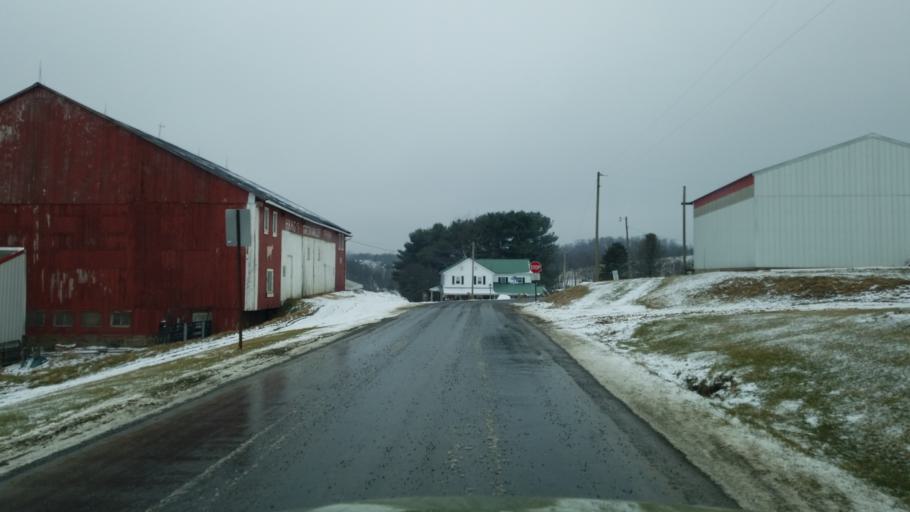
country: US
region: Pennsylvania
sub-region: Jefferson County
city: Sykesville
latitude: 41.0375
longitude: -78.7814
